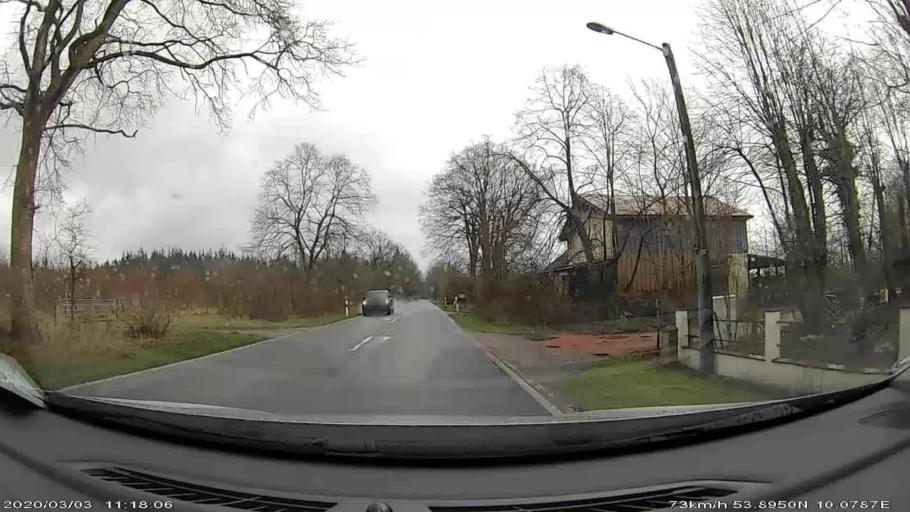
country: DE
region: Schleswig-Holstein
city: Hartenholm
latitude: 53.8932
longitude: 10.0828
